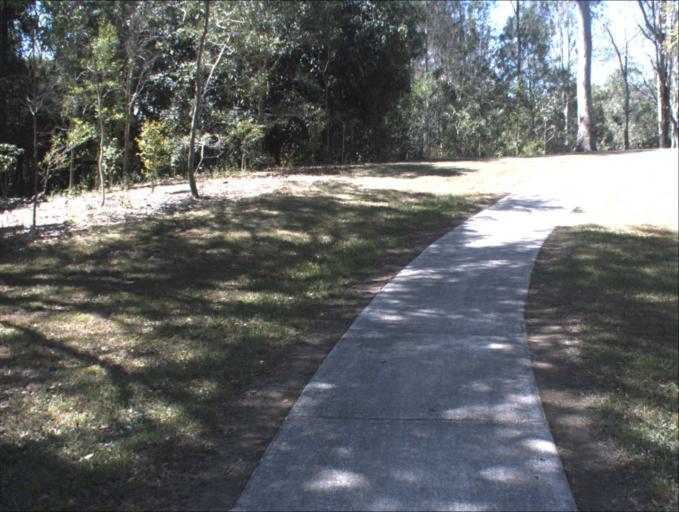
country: AU
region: Queensland
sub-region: Logan
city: Windaroo
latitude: -27.7383
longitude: 153.1994
